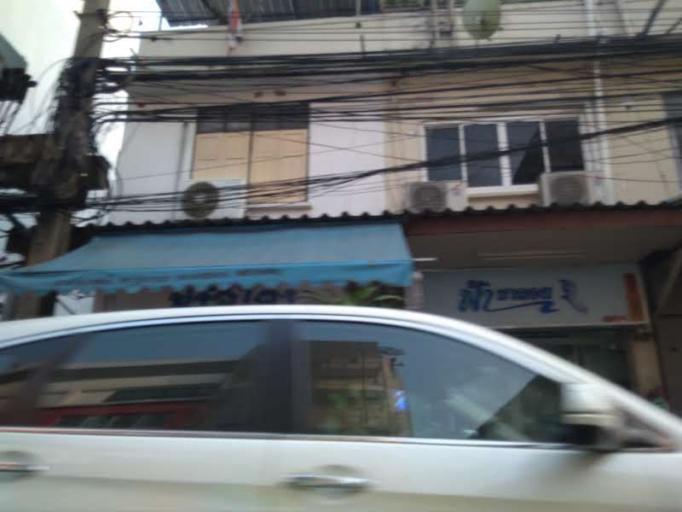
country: TH
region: Bangkok
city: Bangkok
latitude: 13.7537
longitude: 100.4995
